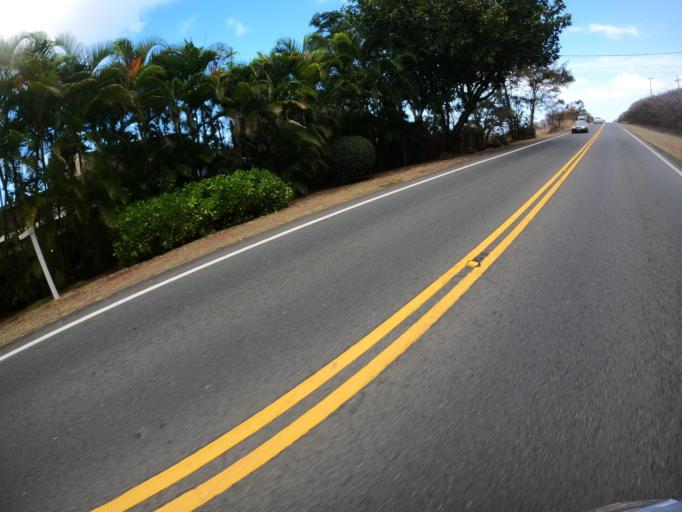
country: US
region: Hawaii
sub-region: Honolulu County
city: Waimanalo Beach
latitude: 21.3226
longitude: -157.6764
